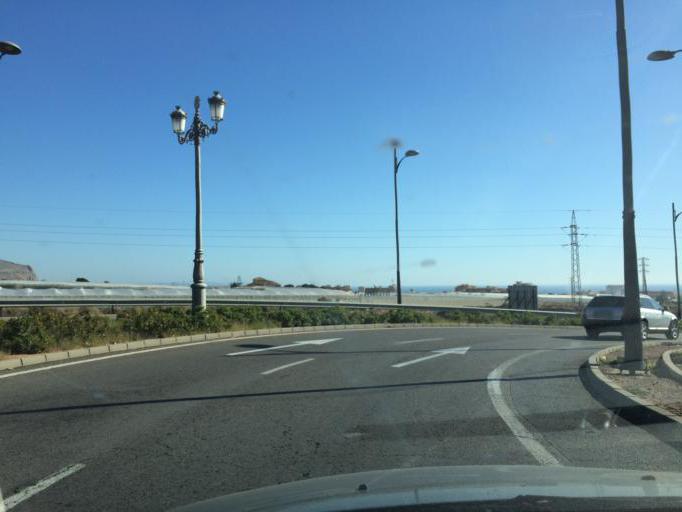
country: ES
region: Andalusia
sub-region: Provincia de Almeria
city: Aguadulce
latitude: 36.8156
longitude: -2.5992
